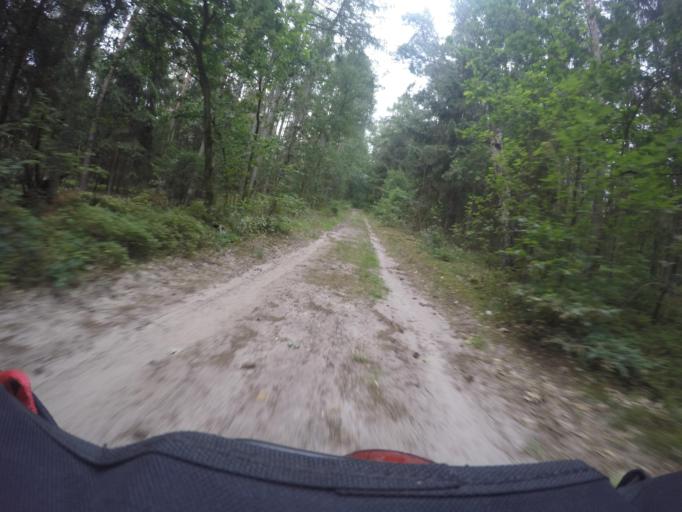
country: DE
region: Lower Saxony
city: Thomasburg
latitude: 53.2173
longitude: 10.6791
